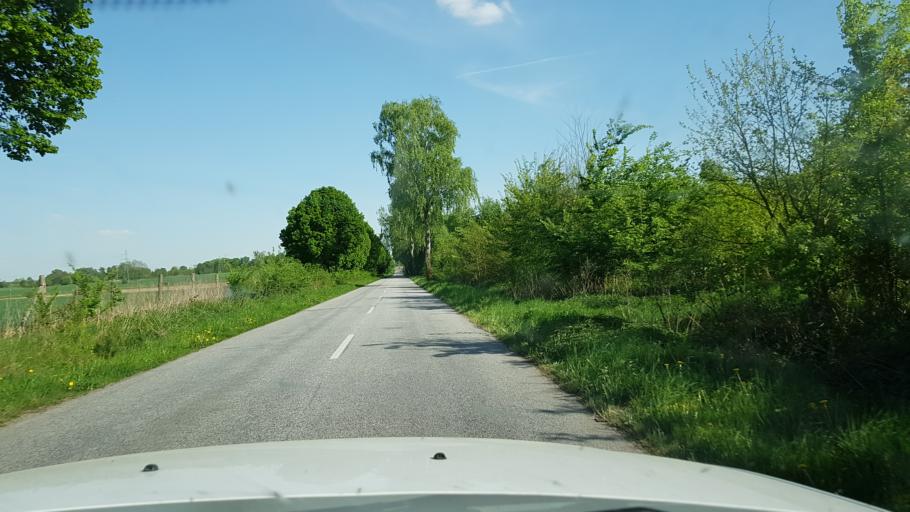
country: PL
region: West Pomeranian Voivodeship
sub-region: Powiat lobeski
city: Resko
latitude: 53.8148
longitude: 15.4015
